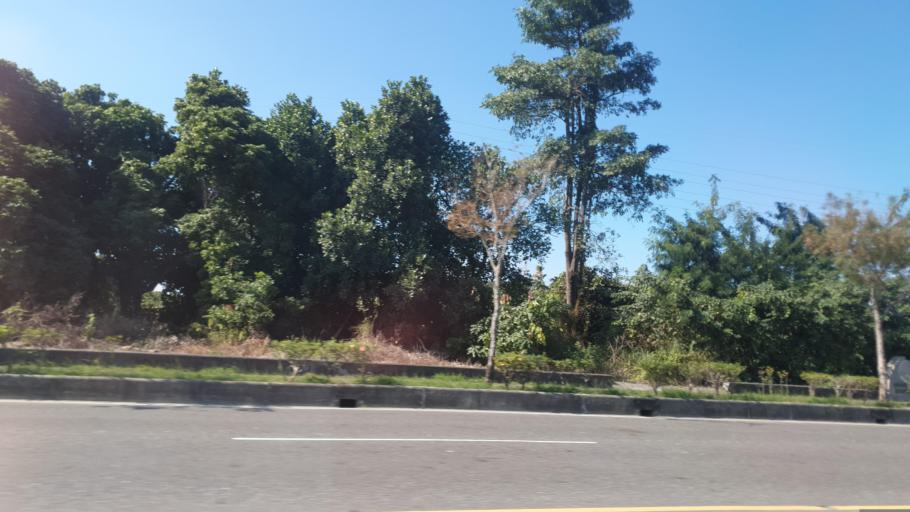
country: TW
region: Taiwan
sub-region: Tainan
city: Tainan
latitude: 23.0327
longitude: 120.3223
